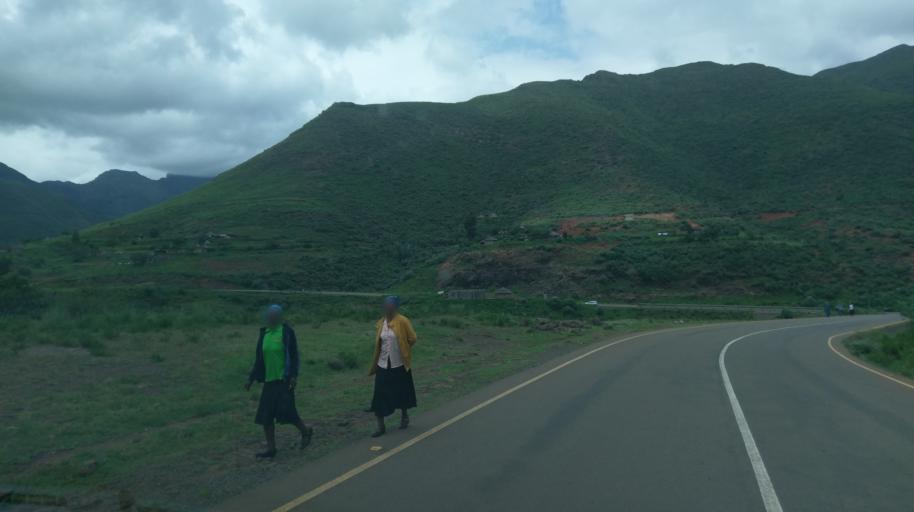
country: LS
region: Butha-Buthe
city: Butha-Buthe
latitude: -29.0460
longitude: 28.3106
